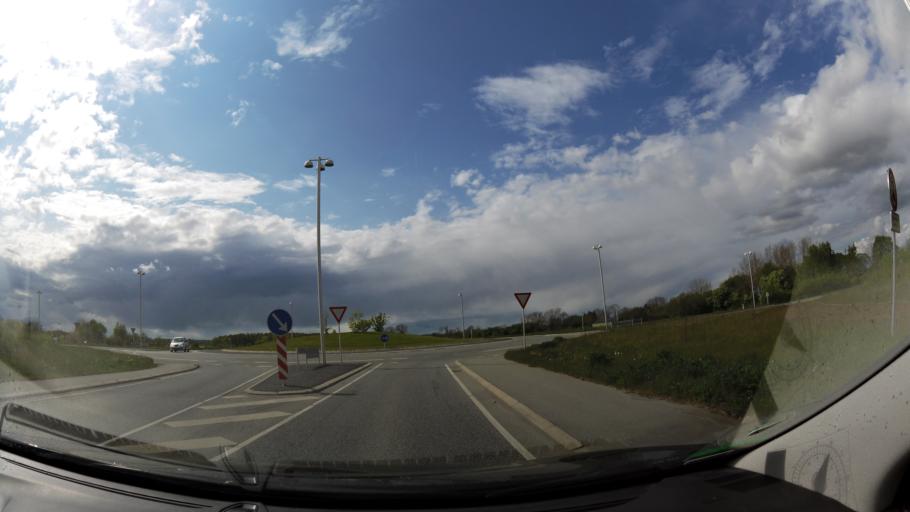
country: DK
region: South Denmark
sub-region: Nyborg Kommune
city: Nyborg
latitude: 55.3211
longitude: 10.7343
